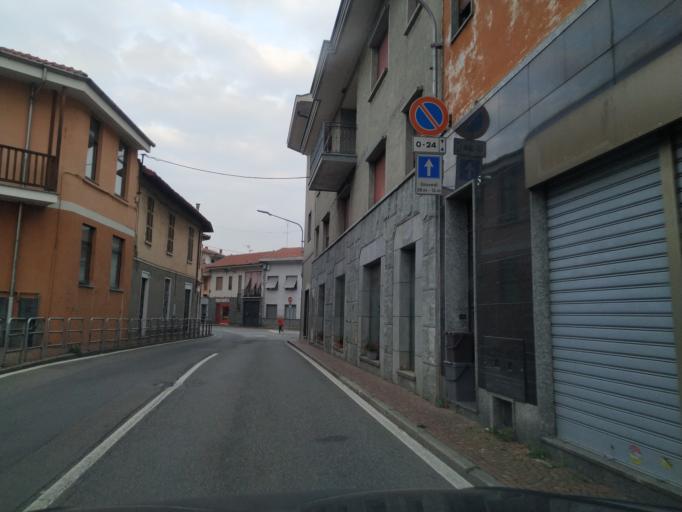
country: IT
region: Piedmont
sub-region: Provincia di Vercelli
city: Cigliano
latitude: 45.3086
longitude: 8.0191
